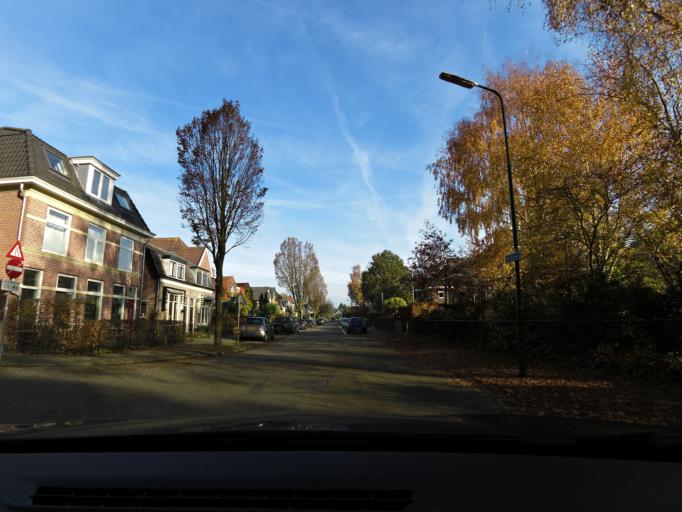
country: NL
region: Utrecht
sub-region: Gemeente De Bilt
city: De Bilt
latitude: 52.1043
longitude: 5.1728
